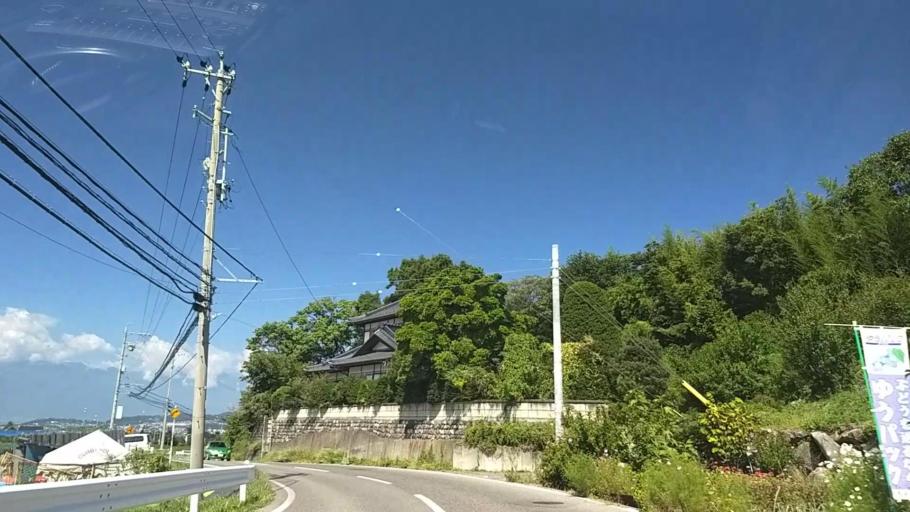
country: JP
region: Nagano
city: Matsumoto
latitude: 36.2333
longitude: 138.0143
